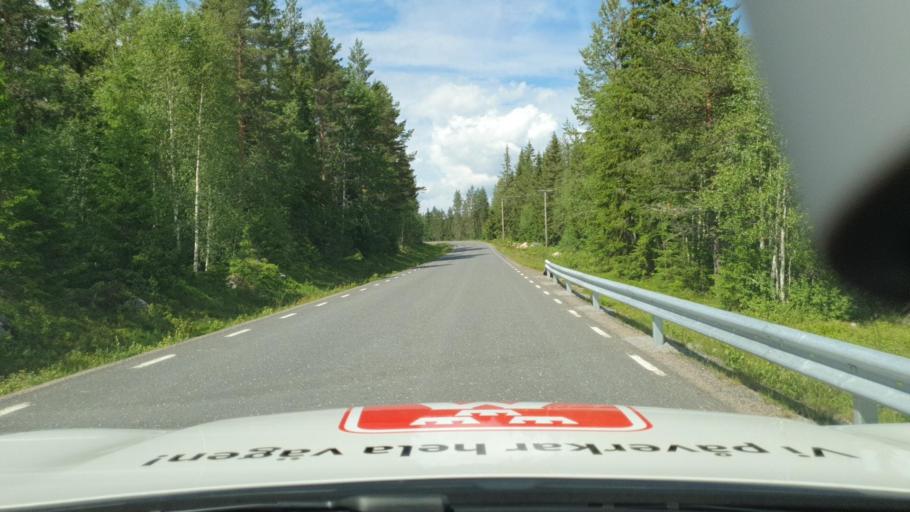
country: SE
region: Vaermland
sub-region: Torsby Kommun
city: Torsby
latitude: 60.5531
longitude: 12.7741
